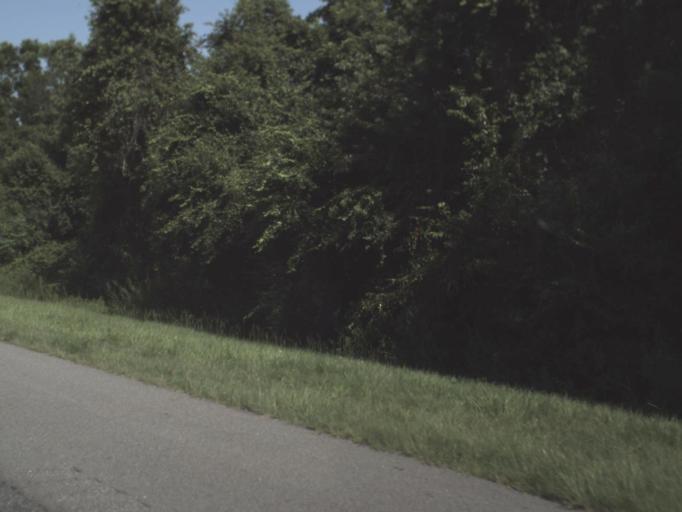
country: US
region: Florida
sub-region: Suwannee County
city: Live Oak
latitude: 30.3522
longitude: -83.0301
